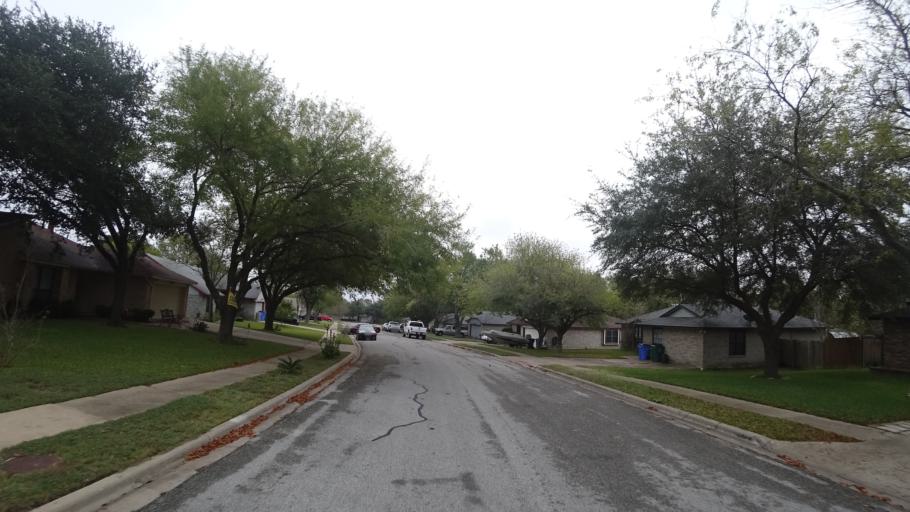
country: US
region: Texas
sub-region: Travis County
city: Pflugerville
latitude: 30.4249
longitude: -97.6108
